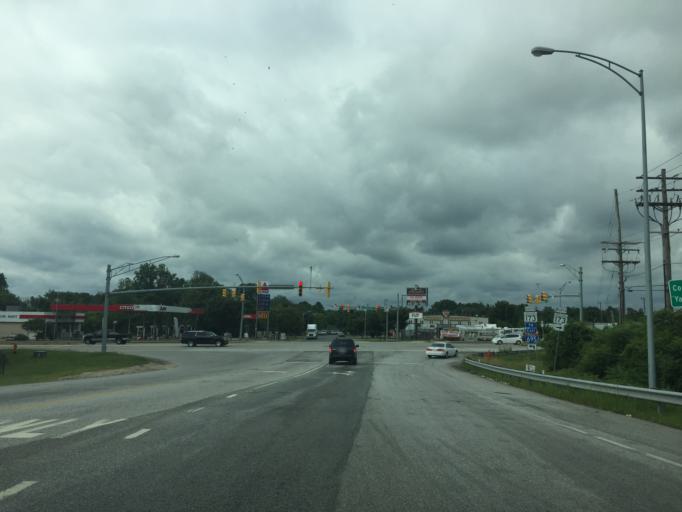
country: US
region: Maryland
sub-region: Anne Arundel County
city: Brooklyn Park
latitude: 39.2040
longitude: -76.5603
